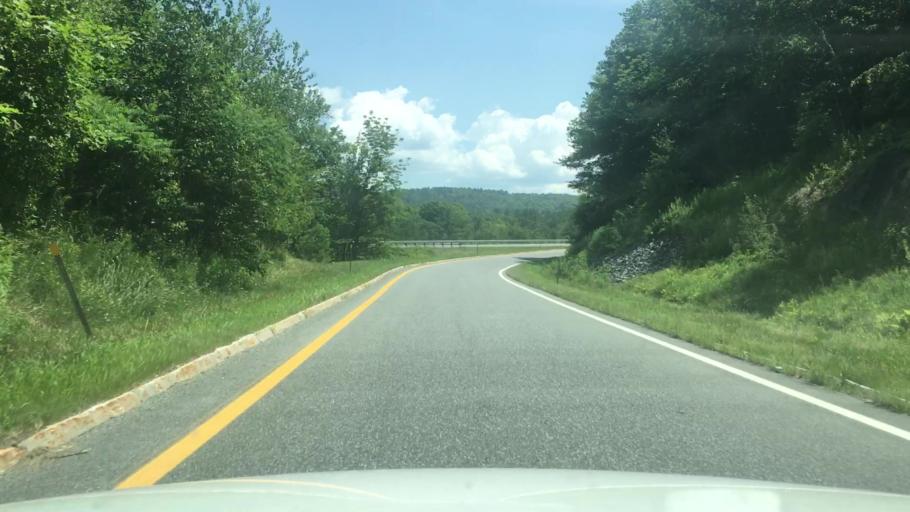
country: US
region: New Hampshire
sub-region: Grafton County
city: Lebanon
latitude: 43.6336
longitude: -72.2127
